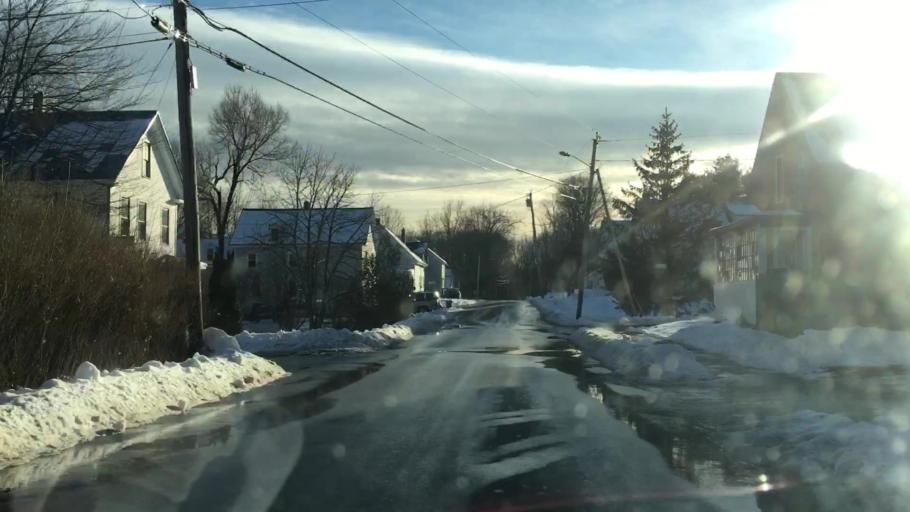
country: US
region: Maine
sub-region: Kennebec County
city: Gardiner
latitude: 44.2306
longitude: -69.7825
